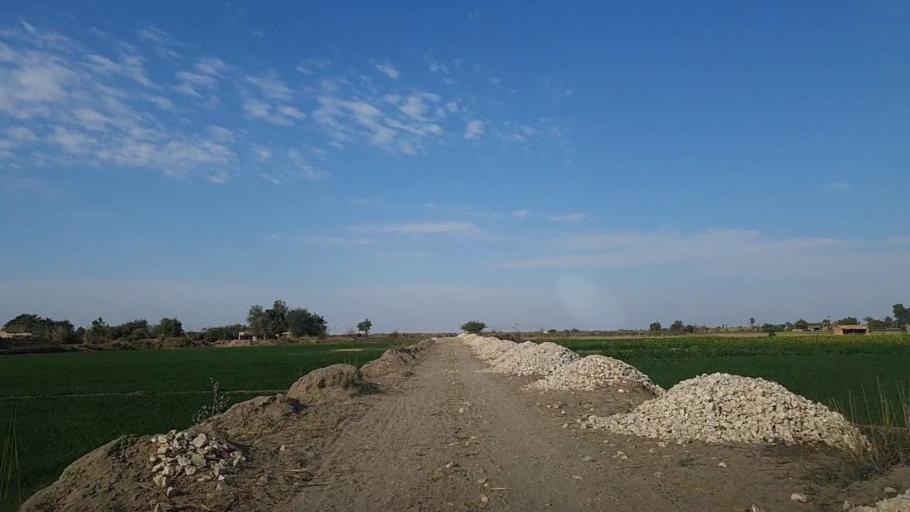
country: PK
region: Sindh
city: Jam Sahib
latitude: 26.3152
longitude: 68.8081
